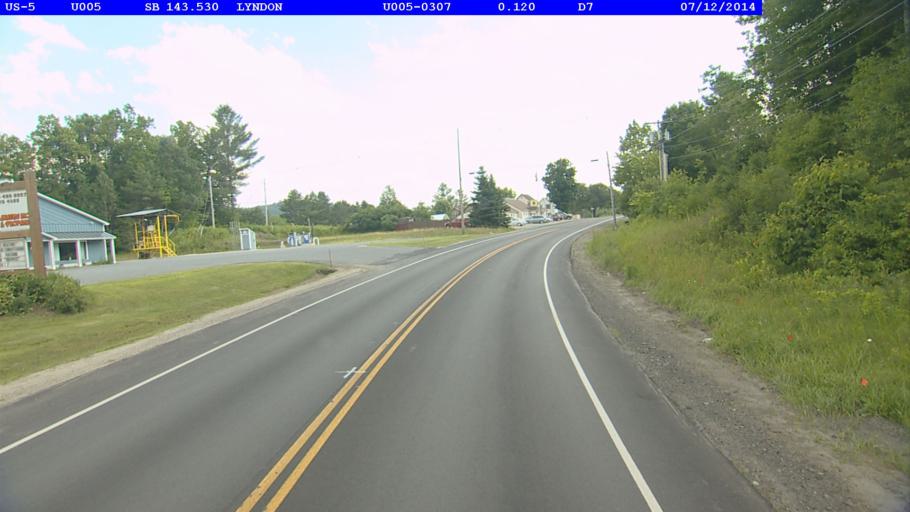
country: US
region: Vermont
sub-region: Caledonia County
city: Lyndon
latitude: 44.5003
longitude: -72.0039
